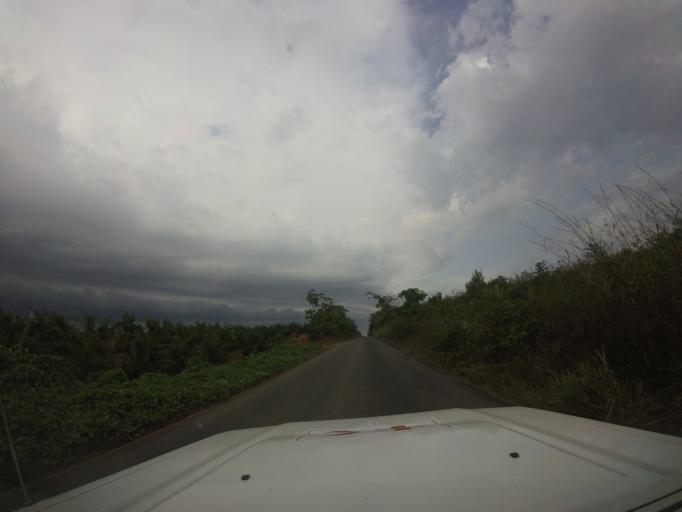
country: LR
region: Bomi
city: Tubmanburg
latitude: 6.7115
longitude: -10.9355
